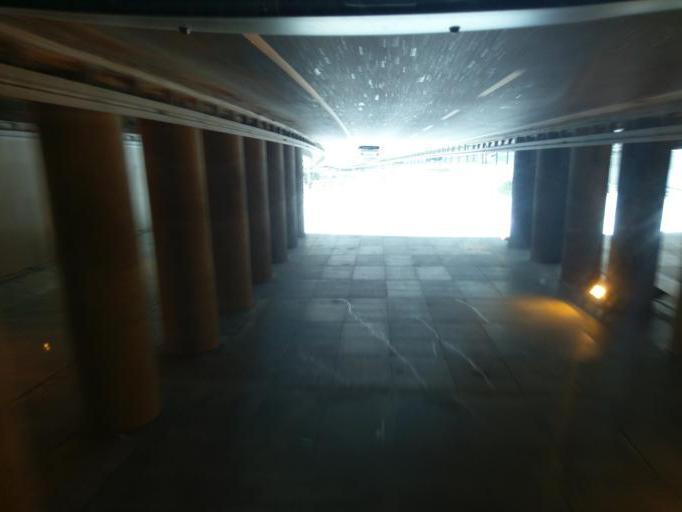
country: TR
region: Istanbul
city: Istanbul
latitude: 41.0013
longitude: 28.9436
